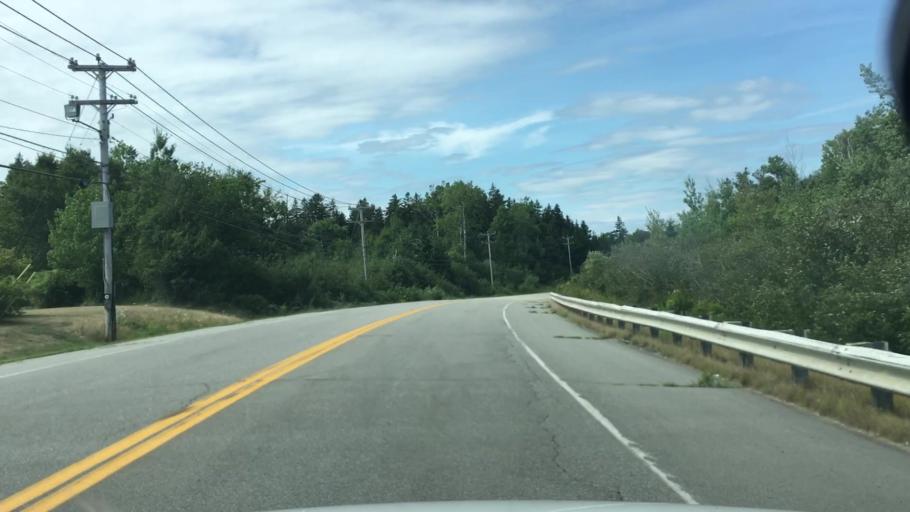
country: US
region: Maine
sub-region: Washington County
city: Eastport
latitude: 44.9280
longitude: -67.0251
